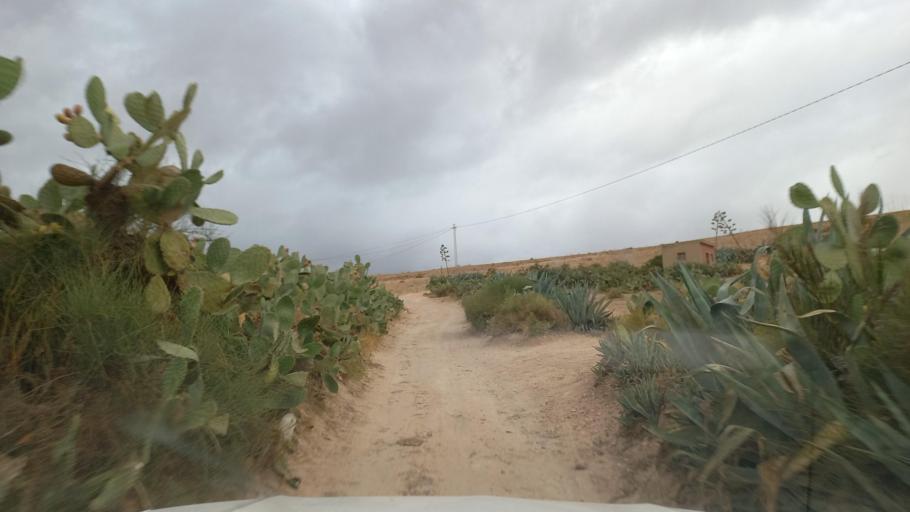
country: TN
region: Al Qasrayn
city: Kasserine
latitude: 35.2757
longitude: 8.9394
